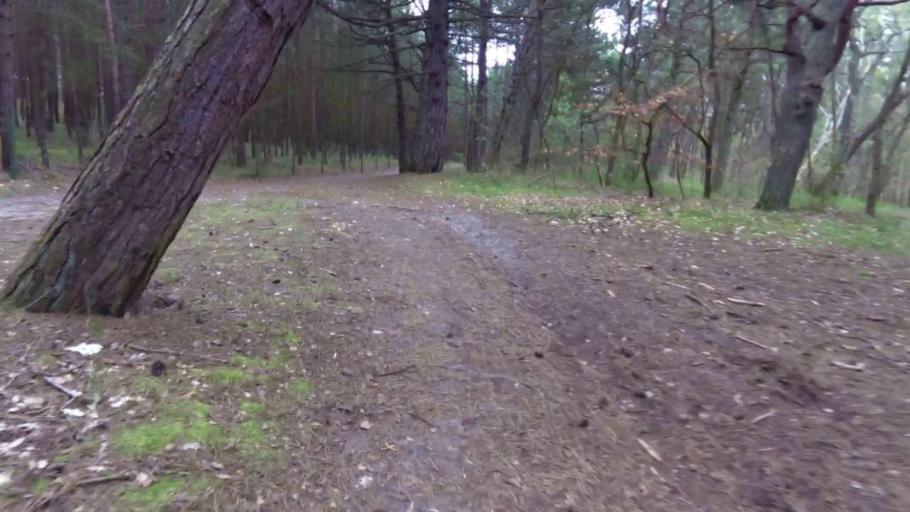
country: PL
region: West Pomeranian Voivodeship
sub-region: Powiat kamienski
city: Dziwnow
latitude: 54.0063
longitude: 14.6843
